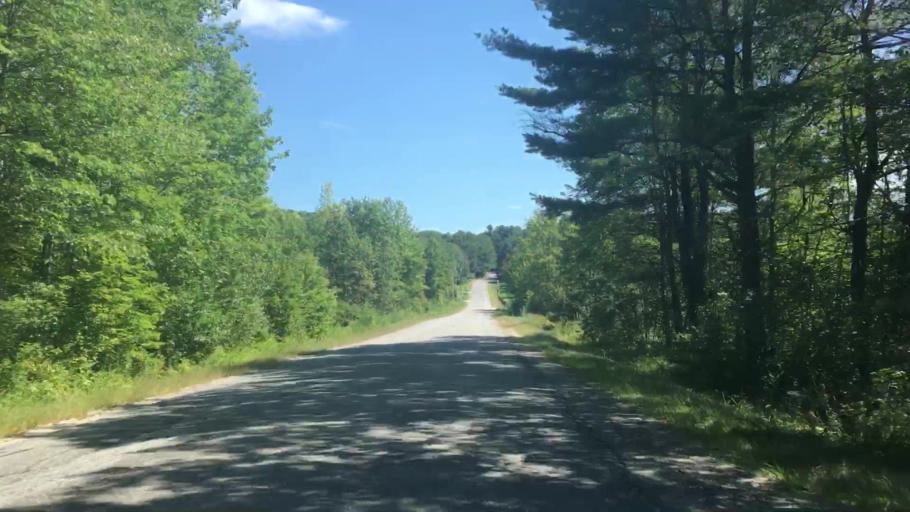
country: US
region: Maine
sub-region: Androscoggin County
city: Sabattus
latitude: 44.1232
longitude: -70.0651
